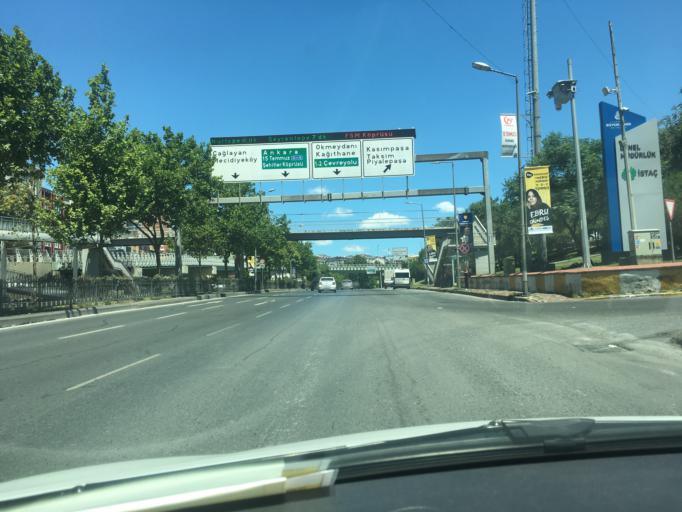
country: TR
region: Istanbul
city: Sisli
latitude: 41.0499
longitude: 28.9681
